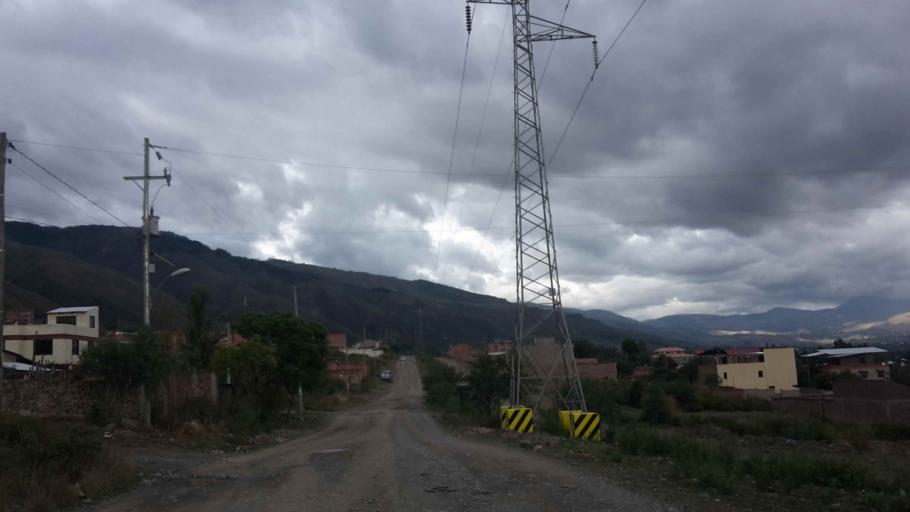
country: BO
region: Cochabamba
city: Cochabamba
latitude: -17.3785
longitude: -66.0663
